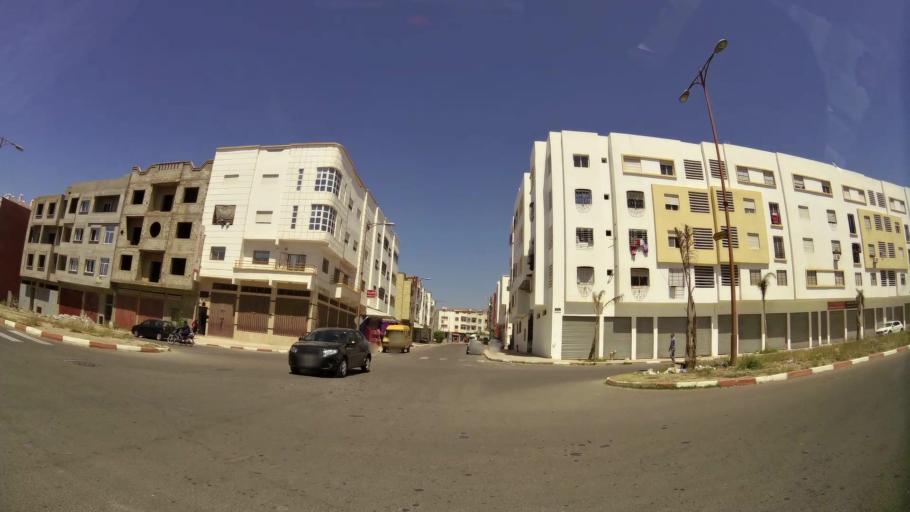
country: MA
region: Oued ed Dahab-Lagouira
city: Dakhla
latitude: 30.4354
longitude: -9.5521
